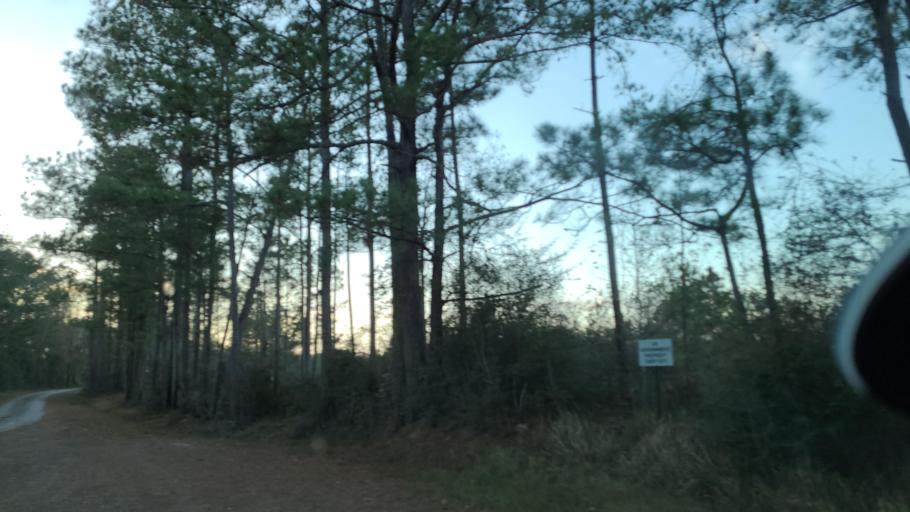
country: US
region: Mississippi
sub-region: Forrest County
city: Hattiesburg
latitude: 31.1715
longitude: -89.2110
